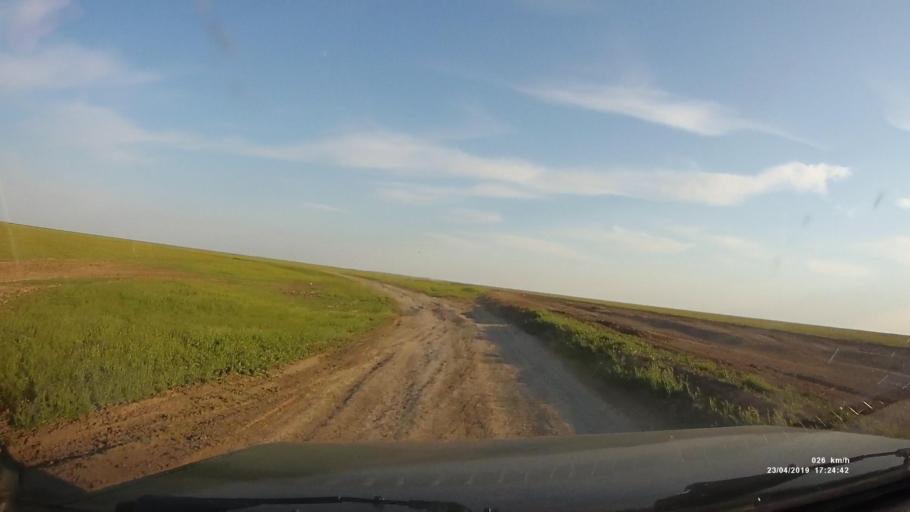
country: RU
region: Kalmykiya
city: Priyutnoye
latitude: 46.1560
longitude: 43.5089
